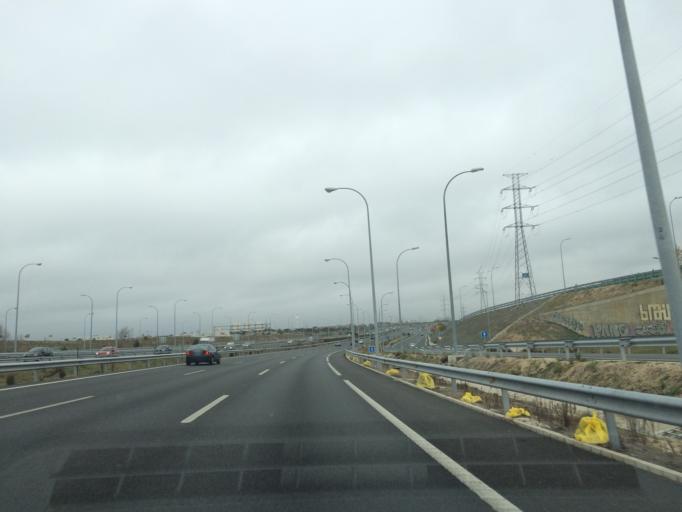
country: ES
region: Madrid
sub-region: Provincia de Madrid
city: Pozuelo de Alarcon
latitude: 40.3990
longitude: -3.8327
